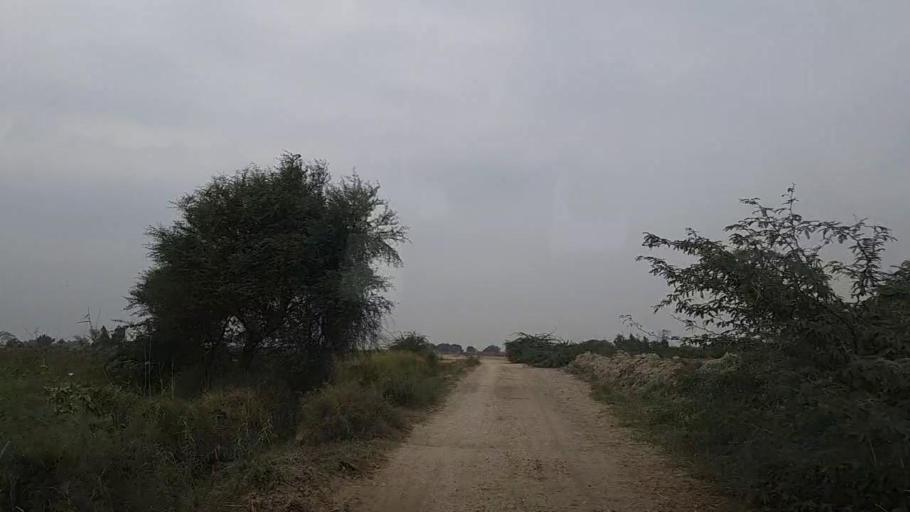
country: PK
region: Sindh
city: Mirpur Sakro
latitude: 24.6145
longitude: 67.7176
